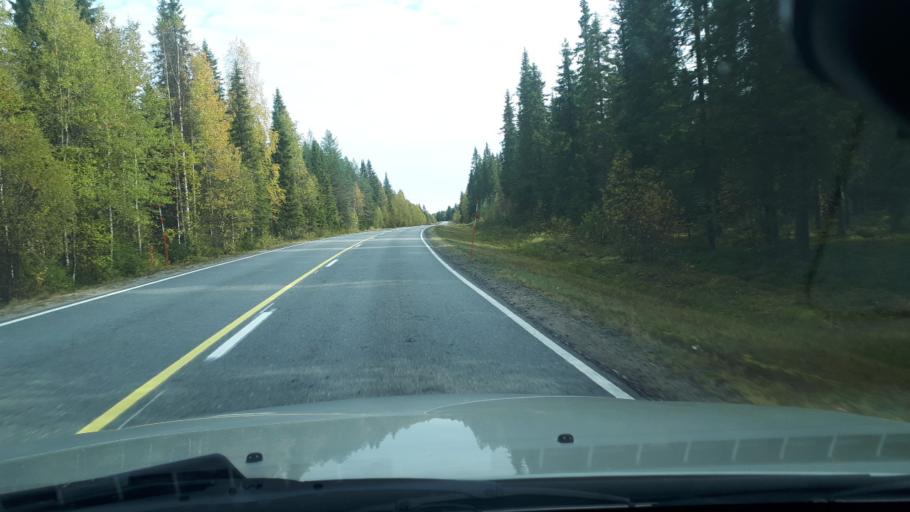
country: FI
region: Lapland
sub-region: Rovaniemi
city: Rovaniemi
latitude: 65.9512
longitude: 25.9124
